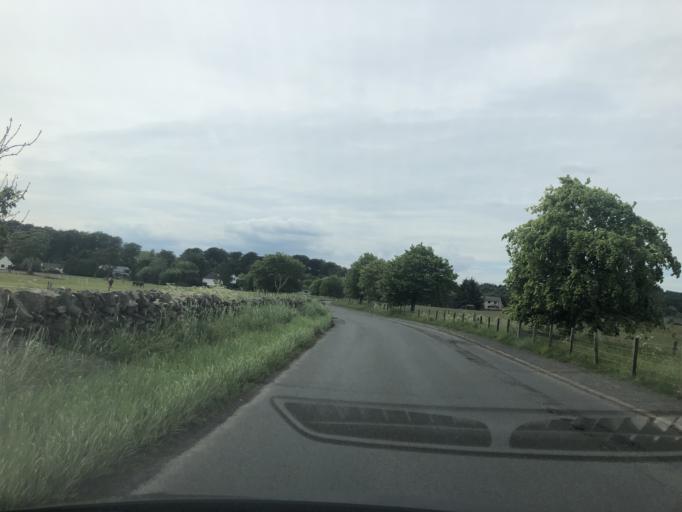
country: GB
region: Scotland
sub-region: The Scottish Borders
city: West Linton
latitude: 55.7459
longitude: -3.3495
